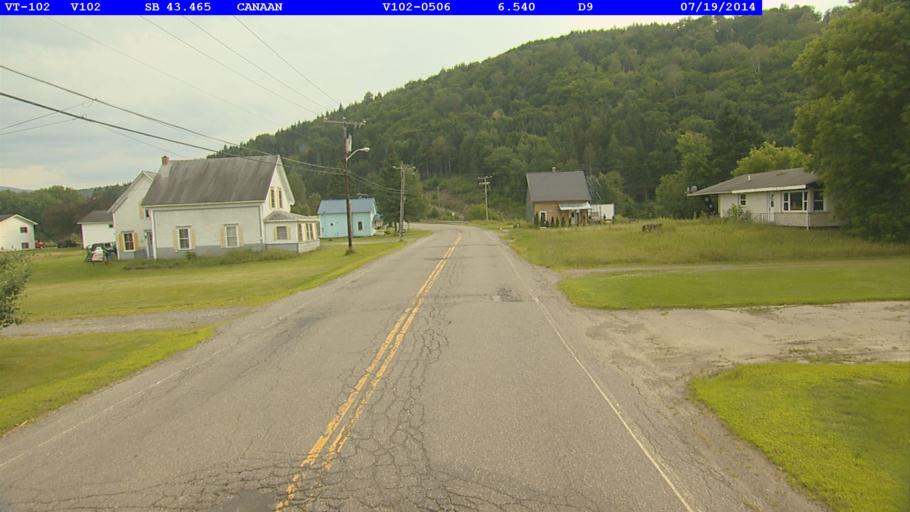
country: US
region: New Hampshire
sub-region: Coos County
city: Colebrook
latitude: 44.9926
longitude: -71.5411
